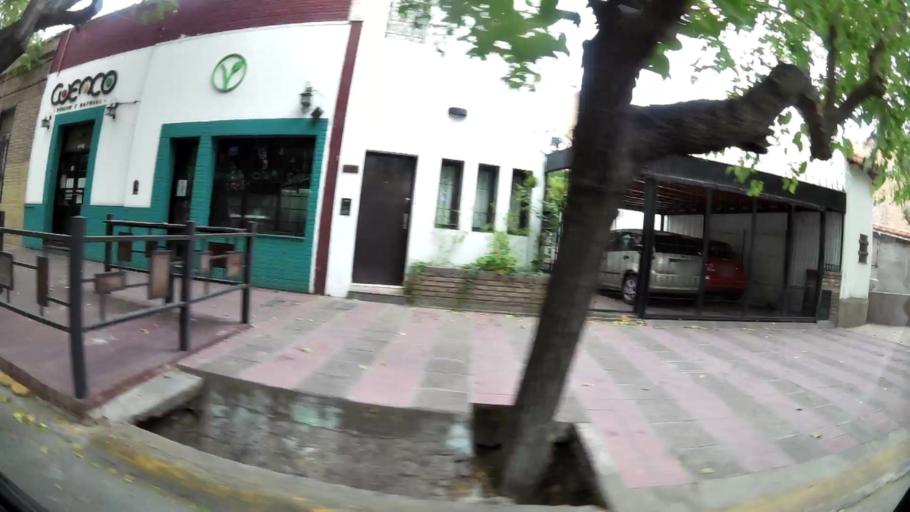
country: AR
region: Mendoza
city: Mendoza
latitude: -32.8847
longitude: -68.8530
